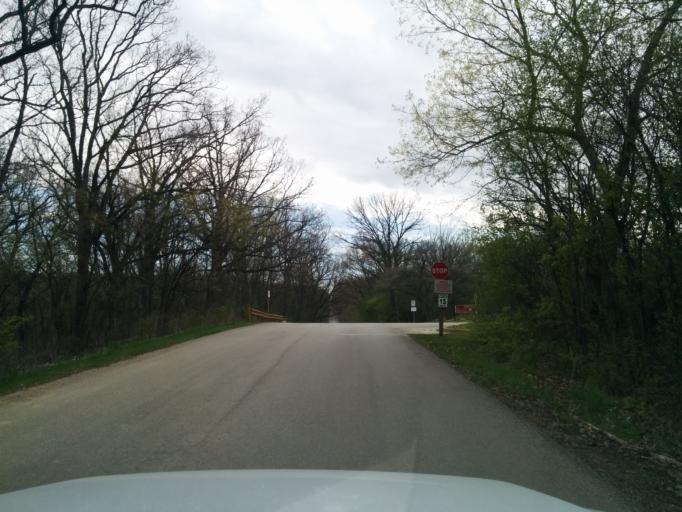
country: US
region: Illinois
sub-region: DuPage County
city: Burr Ridge
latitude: 41.7136
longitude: -87.8951
